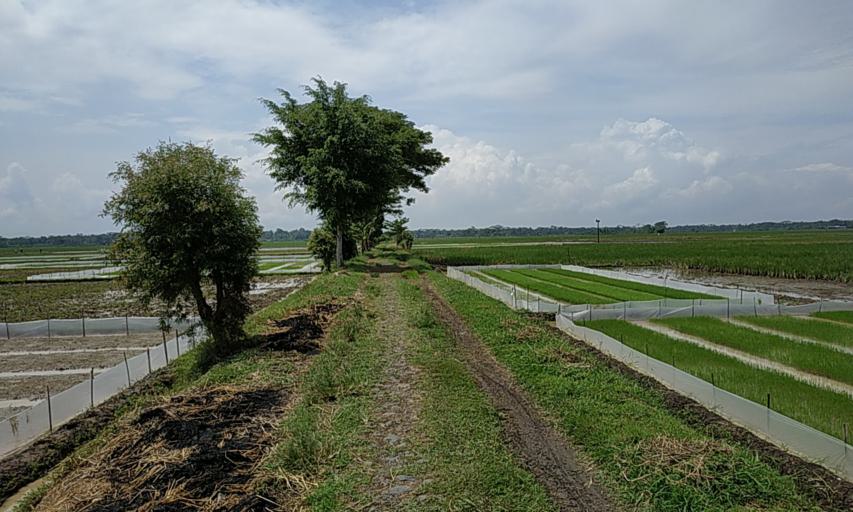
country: ID
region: Central Java
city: Kedungbulu
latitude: -7.5303
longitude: 108.7852
